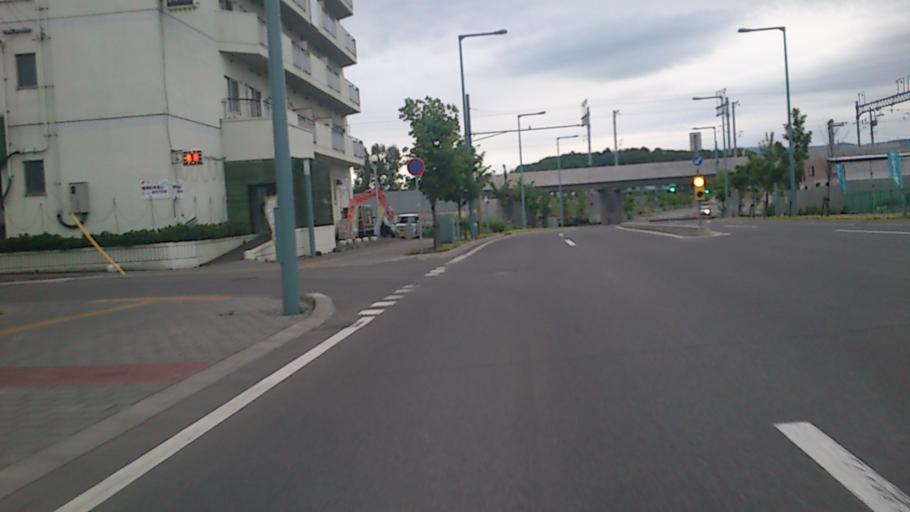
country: JP
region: Hokkaido
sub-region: Asahikawa-shi
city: Asahikawa
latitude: 43.7606
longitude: 142.3706
